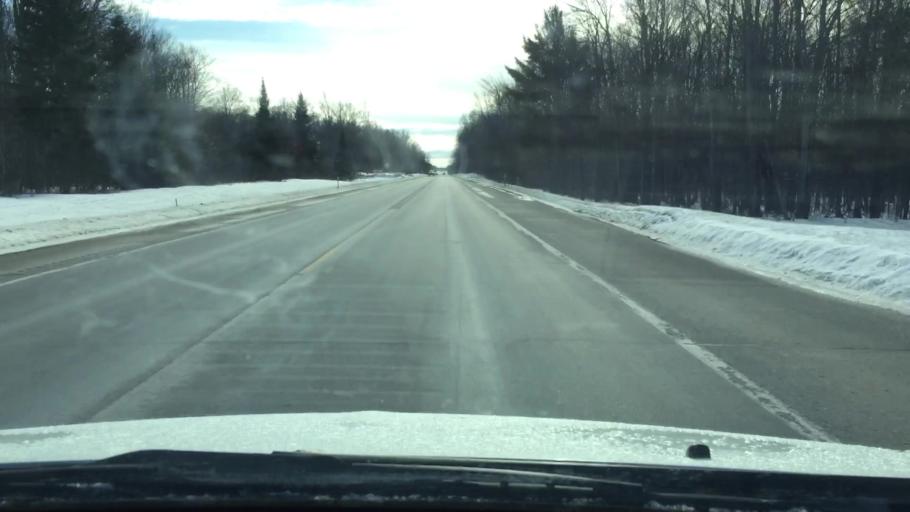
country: US
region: Michigan
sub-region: Kalkaska County
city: Kalkaska
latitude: 44.8263
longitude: -85.1344
